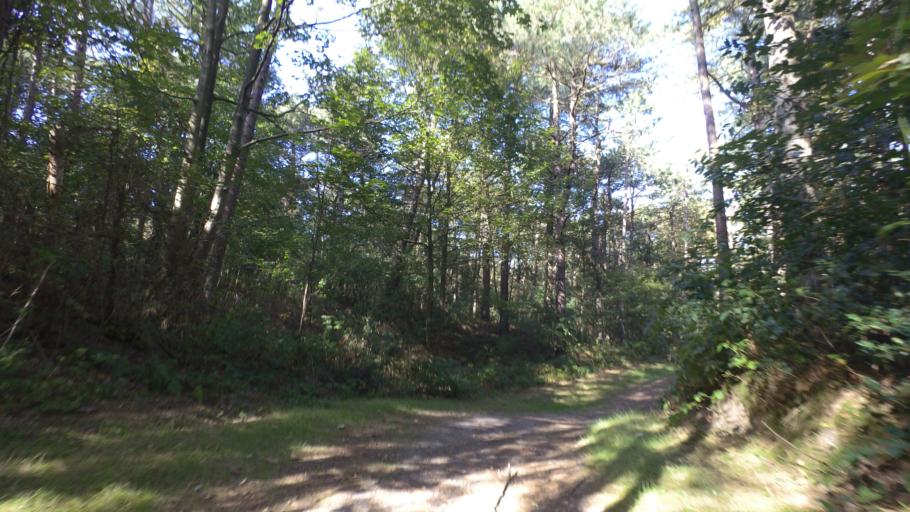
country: NL
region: Friesland
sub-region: Gemeente Ameland
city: Nes
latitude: 53.4529
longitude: 5.7633
